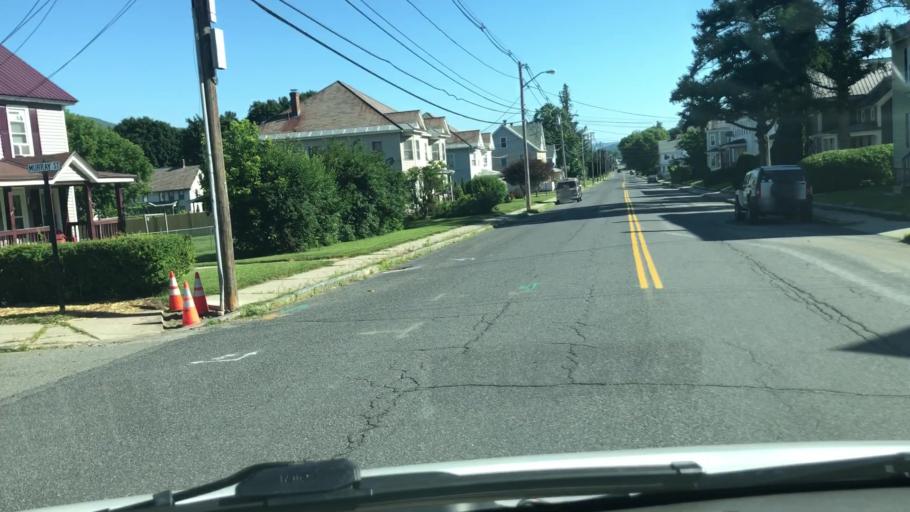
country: US
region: Massachusetts
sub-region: Berkshire County
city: Adams
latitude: 42.6282
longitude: -73.1118
